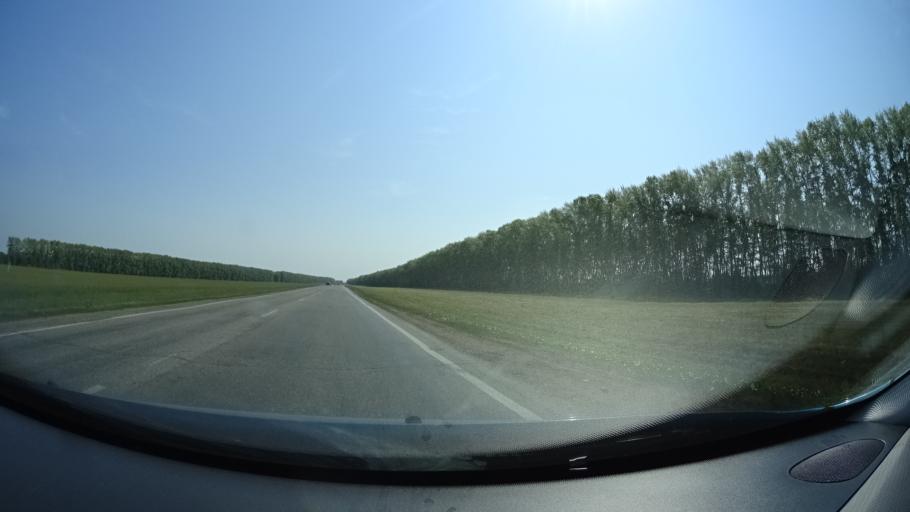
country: RU
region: Bashkortostan
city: Karmaskaly
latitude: 54.3979
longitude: 56.1012
